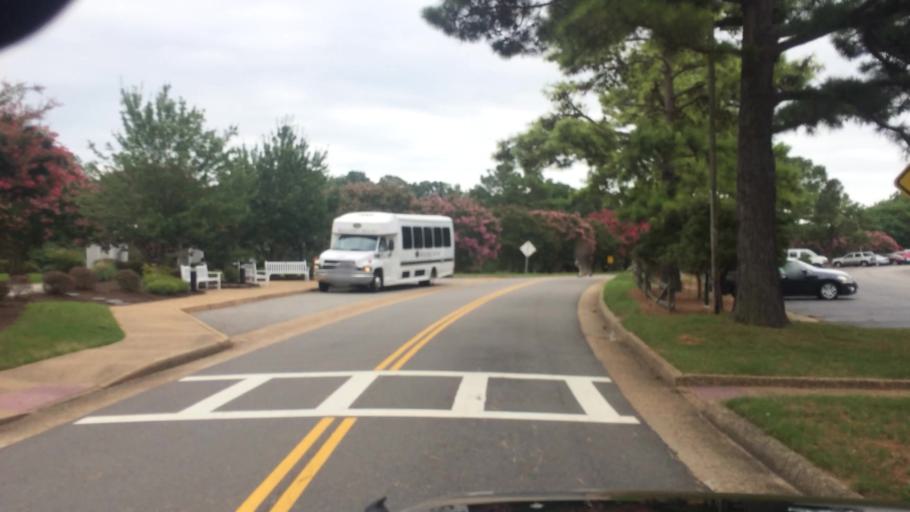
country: US
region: Virginia
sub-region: City of Williamsburg
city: Williamsburg
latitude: 37.2267
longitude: -76.6657
